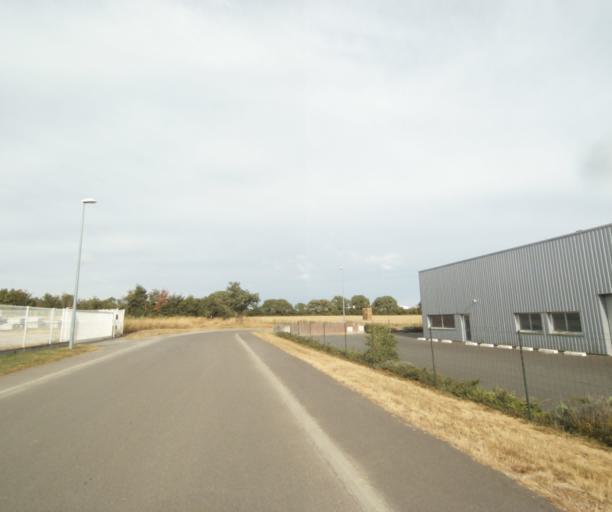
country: FR
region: Pays de la Loire
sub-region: Departement de la Vendee
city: Chateau-d'Olonne
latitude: 46.4950
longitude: -1.7305
